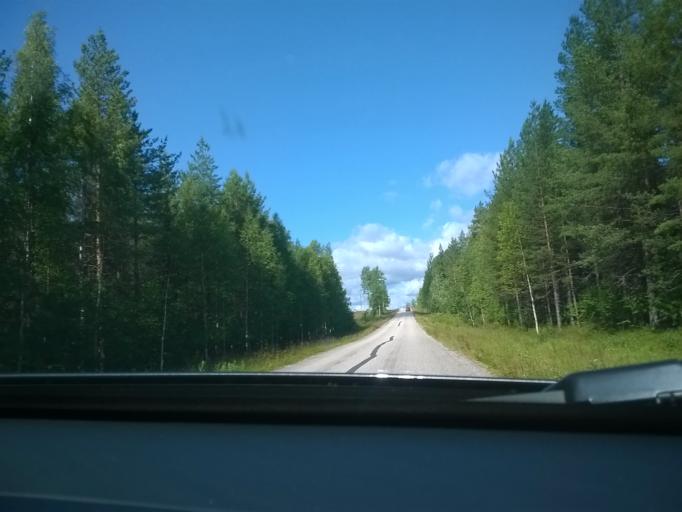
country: FI
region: Kainuu
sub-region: Kehys-Kainuu
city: Kuhmo
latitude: 64.4547
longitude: 29.6555
